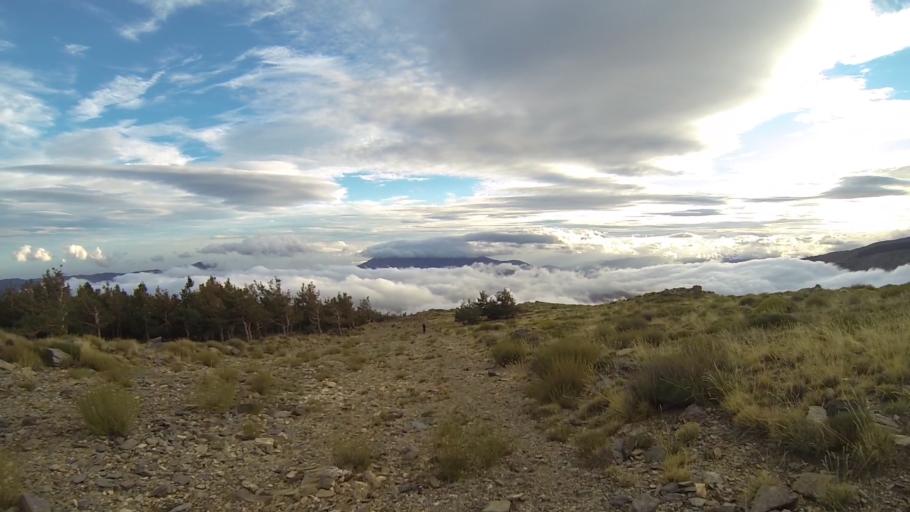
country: ES
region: Andalusia
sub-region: Provincia de Granada
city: Capileira
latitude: 36.9726
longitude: -3.3346
